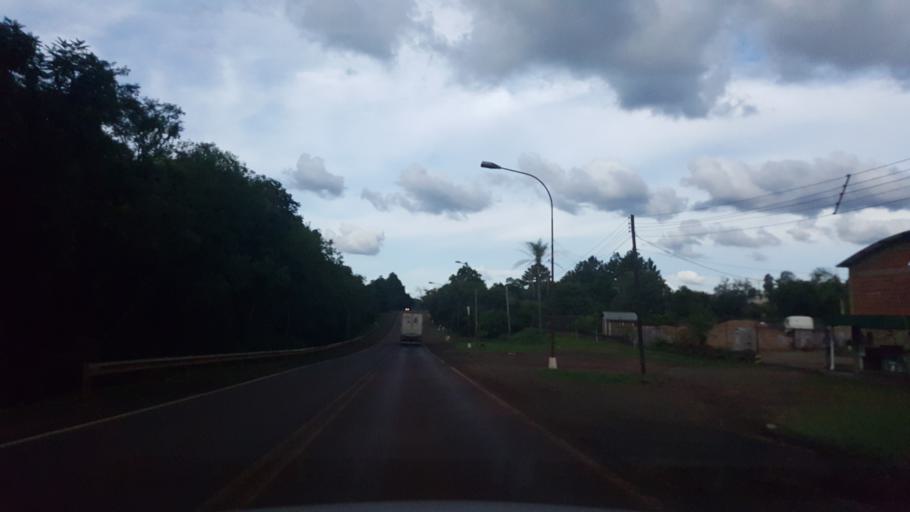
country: AR
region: Misiones
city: Gobernador Roca
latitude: -27.1835
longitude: -55.4616
